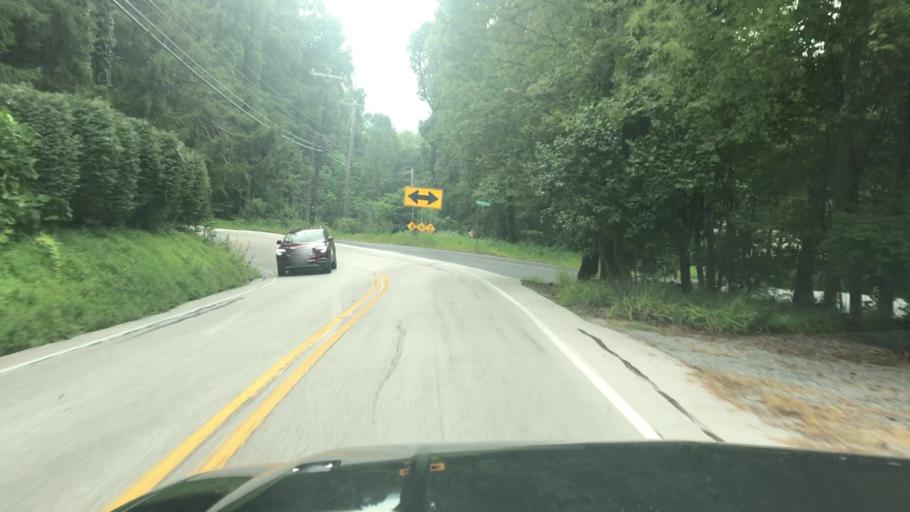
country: US
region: Pennsylvania
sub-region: Cumberland County
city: New Cumberland
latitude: 40.1847
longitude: -76.8734
